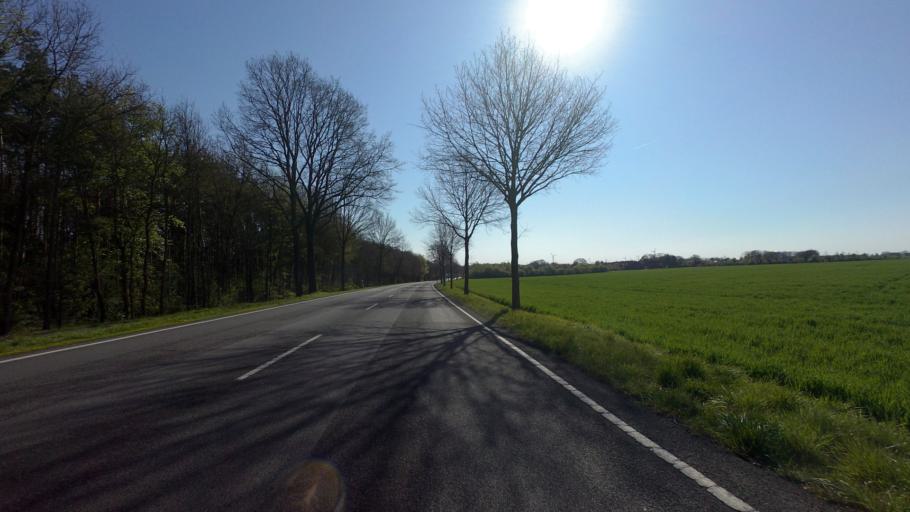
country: DE
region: Lower Saxony
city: Steimbke
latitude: 52.6573
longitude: 9.3760
